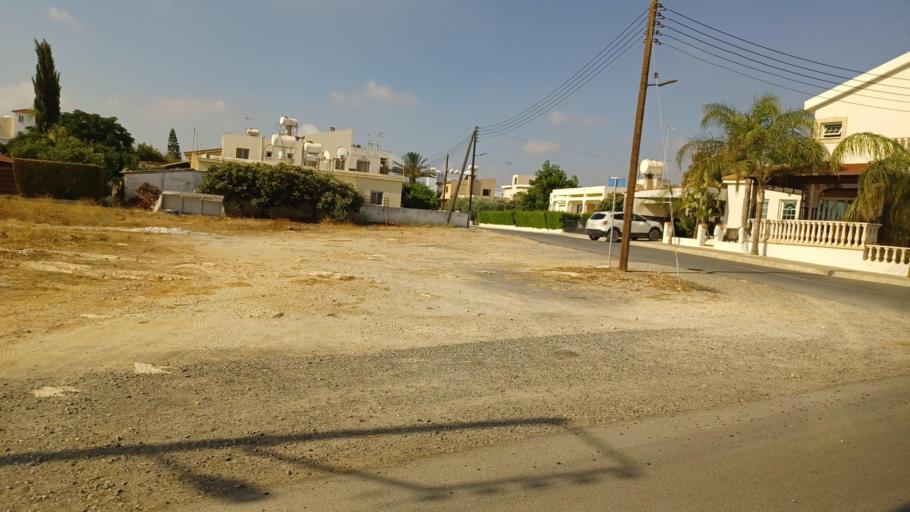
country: CY
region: Ammochostos
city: Deryneia
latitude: 35.0659
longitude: 33.9620
